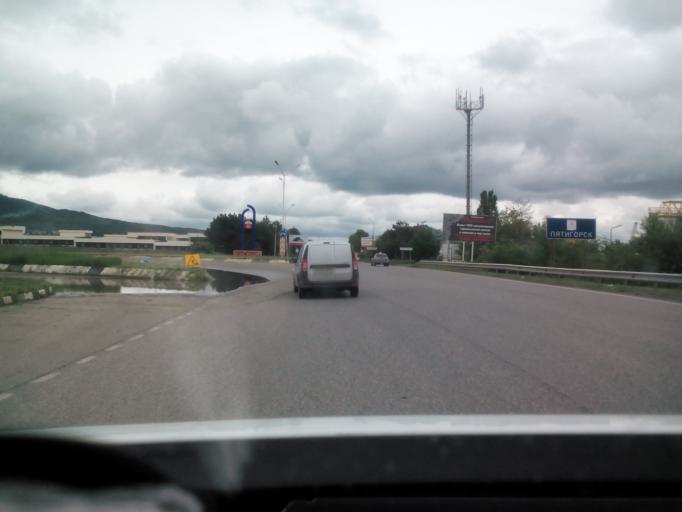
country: RU
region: Stavropol'skiy
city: Vinsady
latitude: 44.0576
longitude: 42.9588
